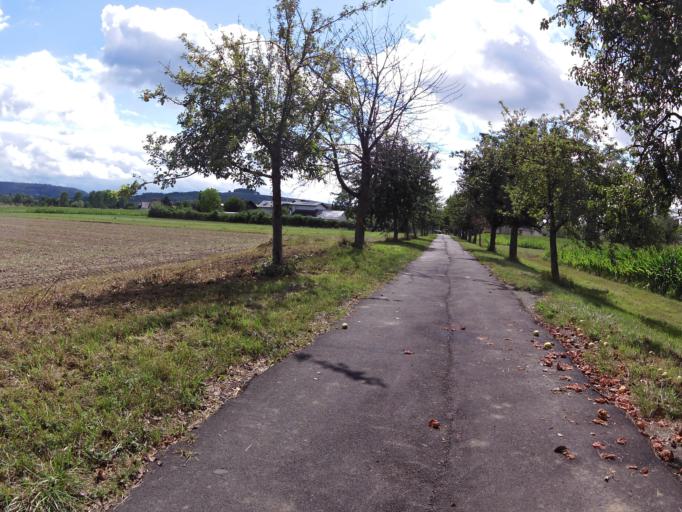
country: DE
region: Baden-Wuerttemberg
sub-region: Freiburg Region
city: Lahr
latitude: 48.3674
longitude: 7.8329
